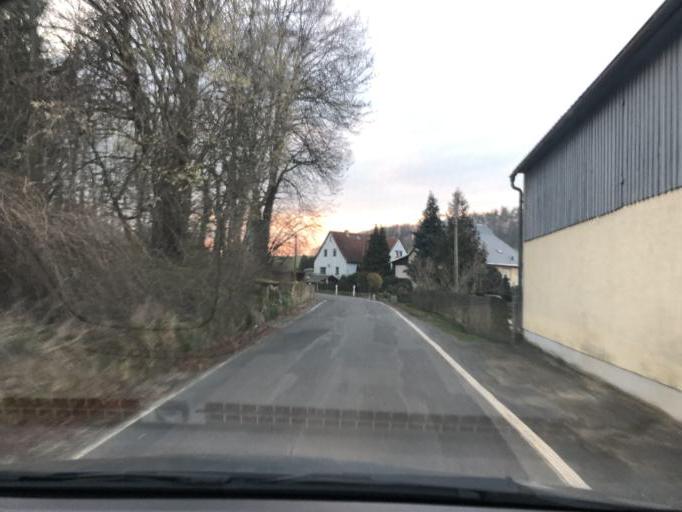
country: DE
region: Saxony
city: Kamenz
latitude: 51.2400
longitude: 14.0830
